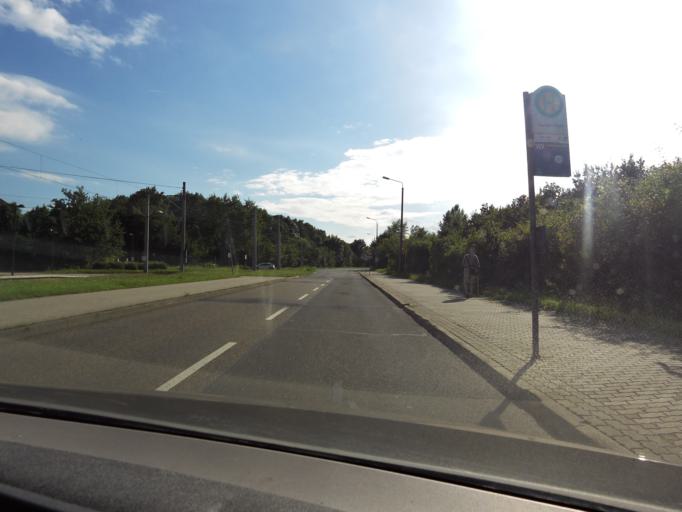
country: DE
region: Saxony
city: Taucha
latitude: 51.3605
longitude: 12.4689
